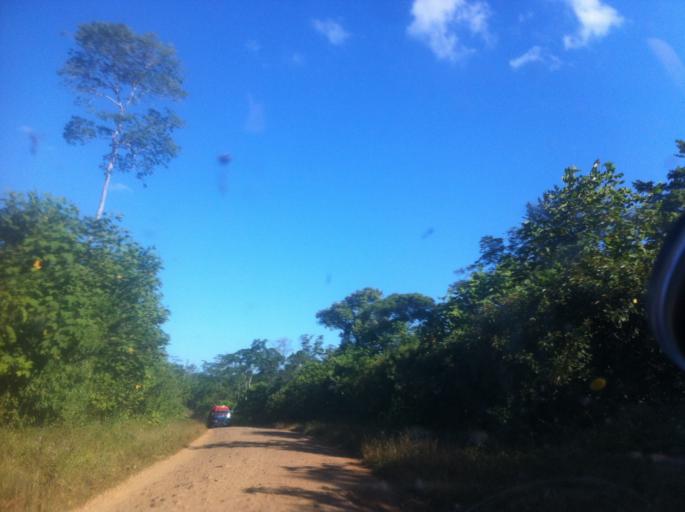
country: CR
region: Alajuela
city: Los Chiles
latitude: 11.0650
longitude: -84.4966
